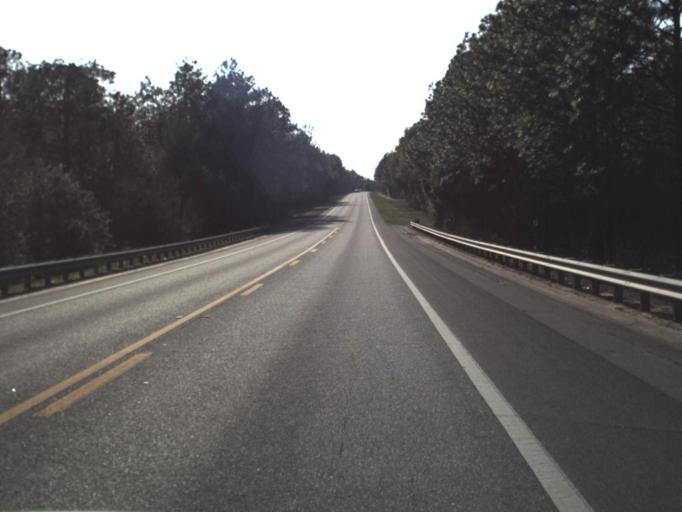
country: US
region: Florida
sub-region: Bay County
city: Youngstown
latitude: 30.4290
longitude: -85.5568
